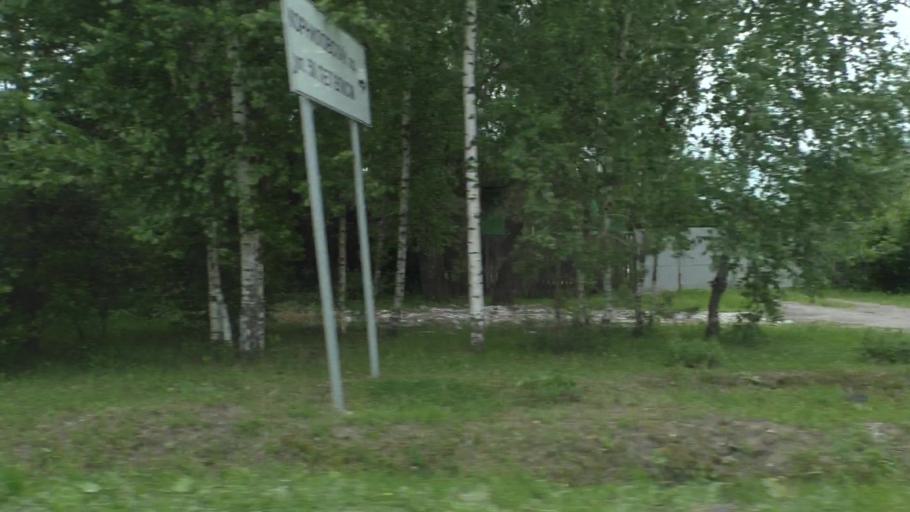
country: RU
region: Moskovskaya
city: Yegor'yevsk
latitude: 55.3975
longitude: 39.0136
